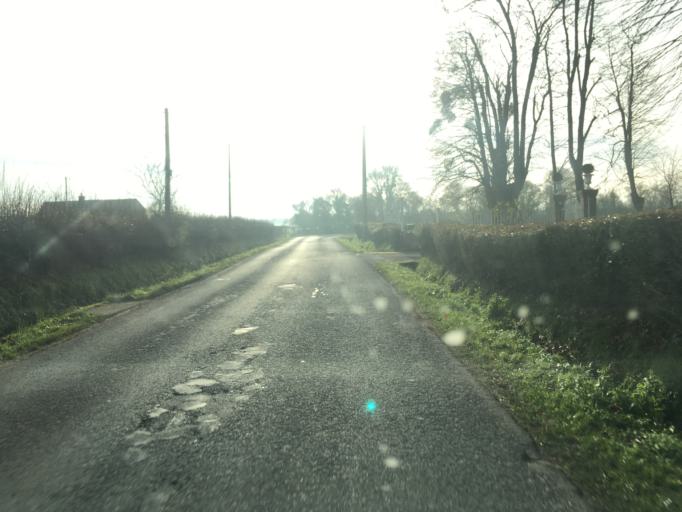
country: FR
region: Lower Normandy
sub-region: Departement du Calvados
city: Dozule
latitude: 49.2029
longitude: -0.0635
